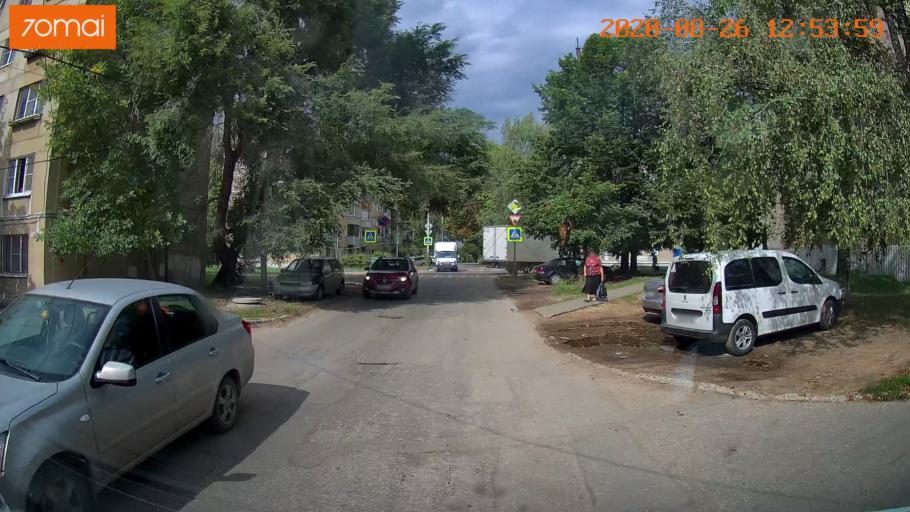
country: RU
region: Rjazan
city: Ryazan'
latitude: 54.6027
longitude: 39.7593
